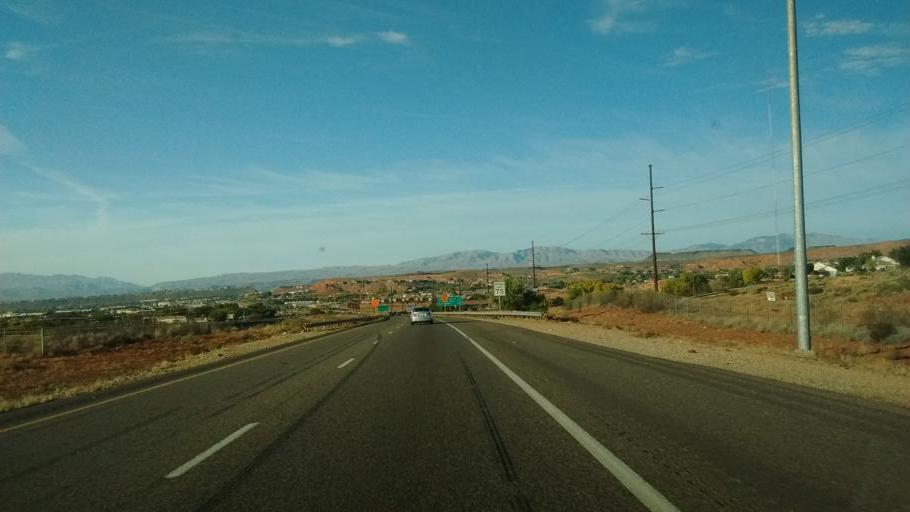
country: US
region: Utah
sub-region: Washington County
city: Washington
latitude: 37.1429
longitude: -113.5007
